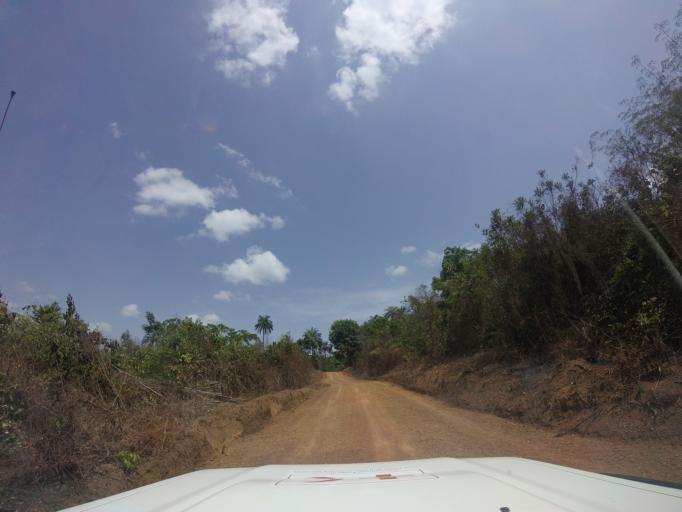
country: SL
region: Southern Province
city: Zimmi
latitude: 7.1248
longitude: -11.2830
